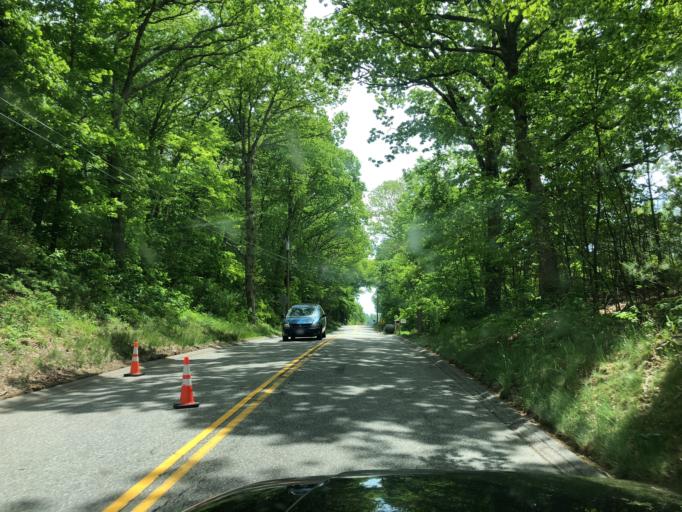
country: US
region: Connecticut
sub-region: Windham County
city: North Grosvenor Dale
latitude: 41.9723
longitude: -71.8820
